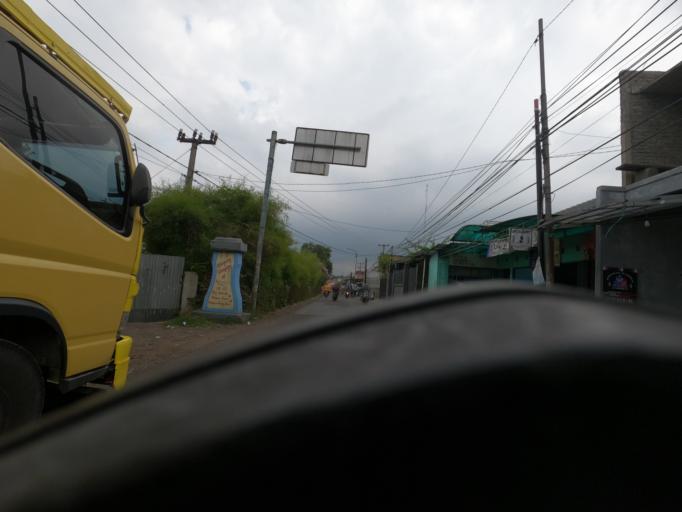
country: ID
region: West Java
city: Cimahi
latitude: -6.8166
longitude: 107.5548
